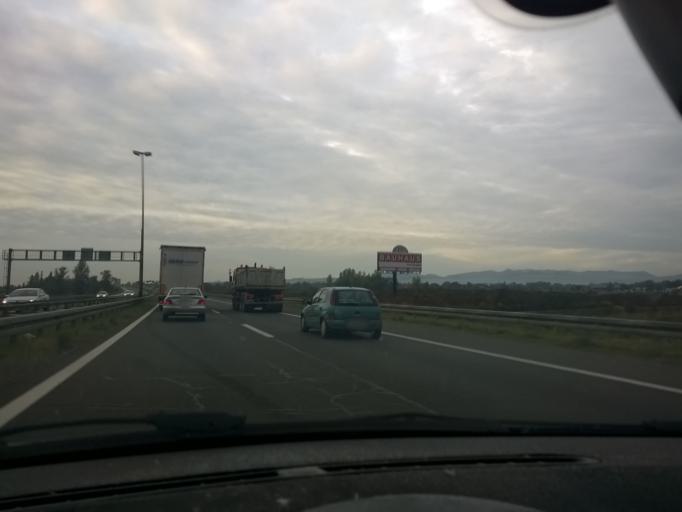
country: HR
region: Zagrebacka
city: Zapresic
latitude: 45.8452
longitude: 15.8223
